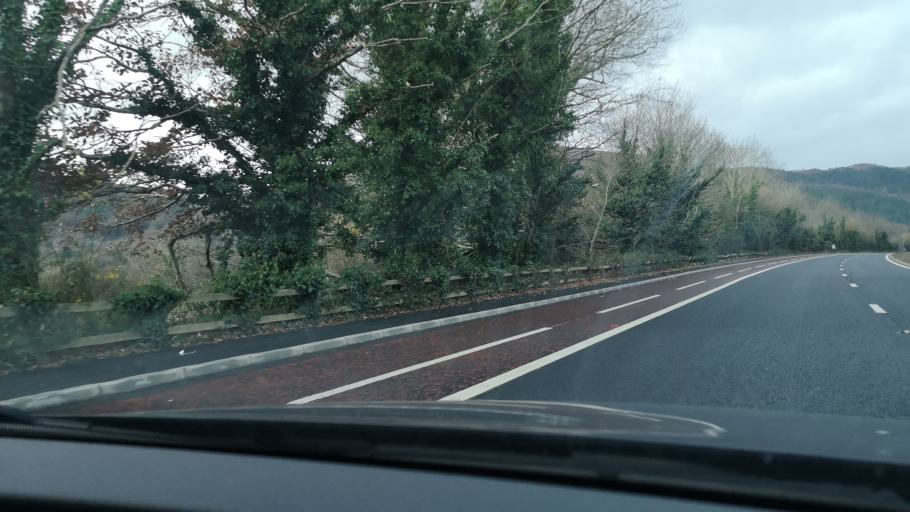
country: GB
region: Northern Ireland
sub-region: Down District
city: Warrenpoint
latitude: 54.1130
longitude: -6.2861
